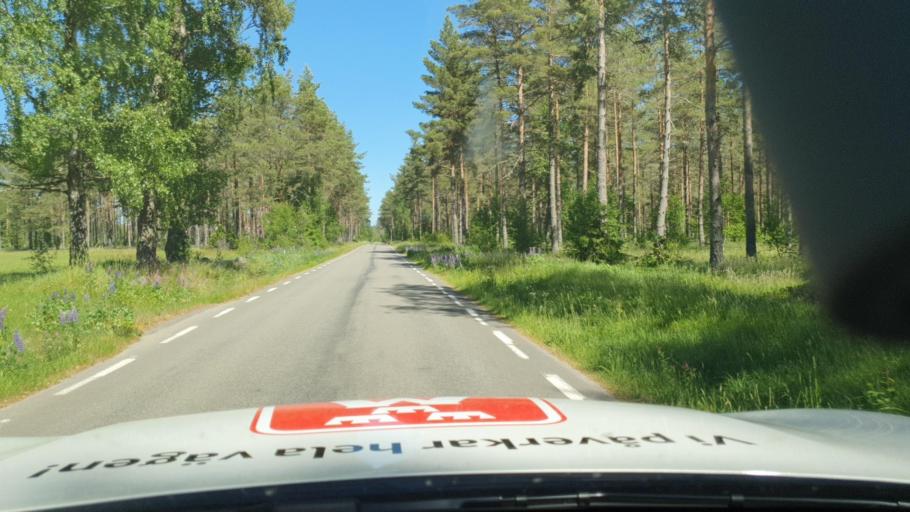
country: SE
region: Joenkoeping
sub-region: Habo Kommun
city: Habo
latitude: 58.0635
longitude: 14.0568
